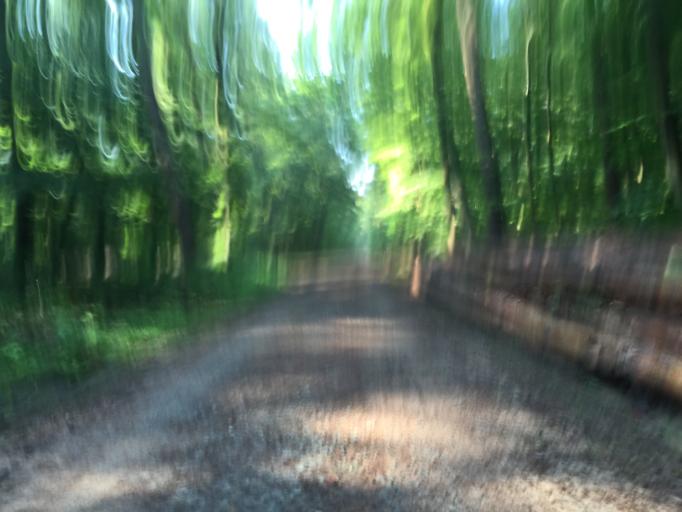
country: DE
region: Hesse
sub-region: Regierungsbezirk Darmstadt
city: Darmstadt
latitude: 49.8523
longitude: 8.6139
